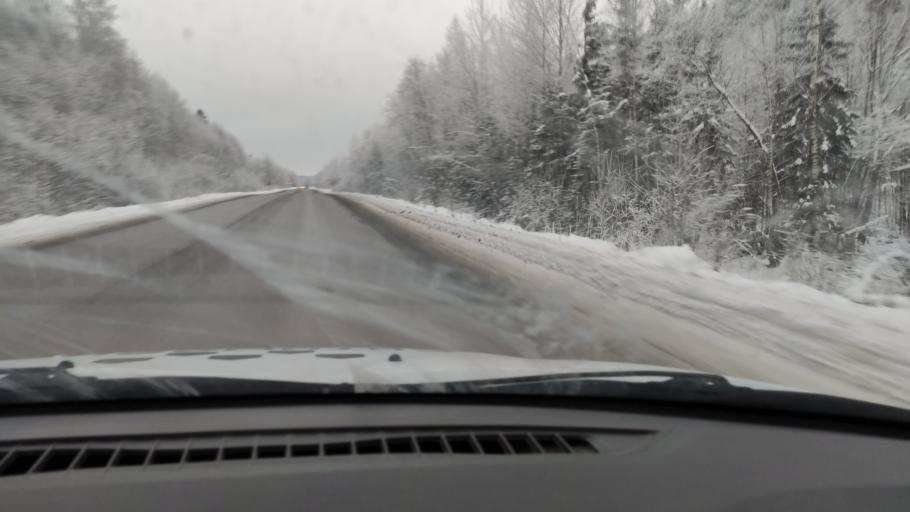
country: RU
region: Perm
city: Novyye Lyady
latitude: 58.0293
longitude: 56.6225
